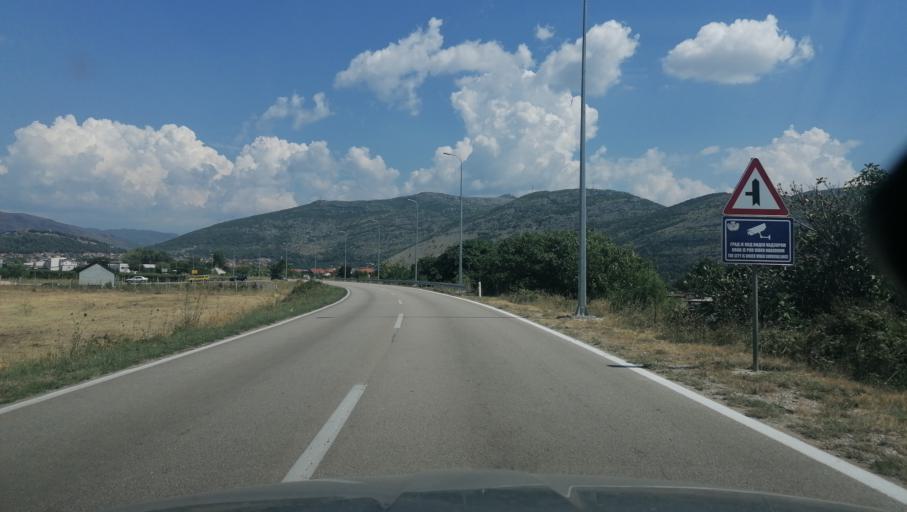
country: BA
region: Republika Srpska
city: Trebinje
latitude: 42.7030
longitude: 18.3269
